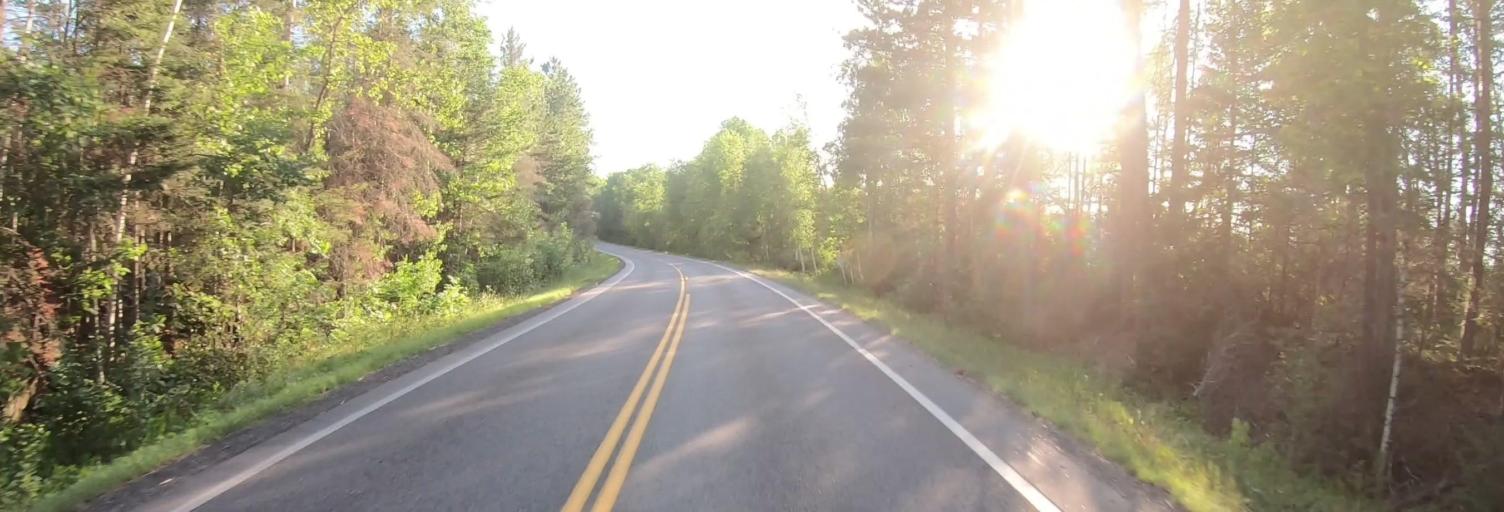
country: US
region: Minnesota
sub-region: Saint Louis County
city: Ely
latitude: 47.9320
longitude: -91.7173
